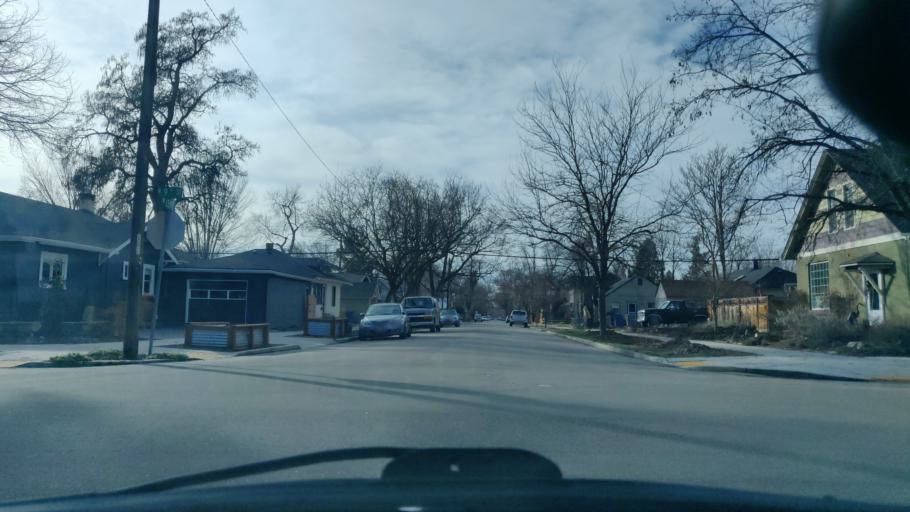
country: US
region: Idaho
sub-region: Ada County
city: Boise
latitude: 43.6328
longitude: -116.1987
